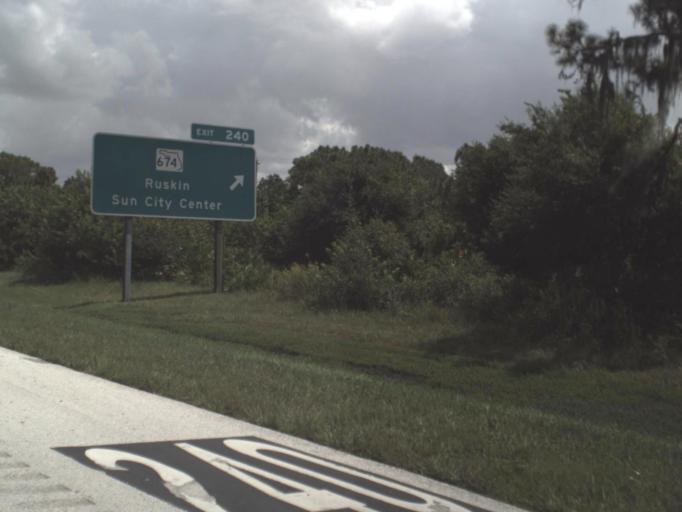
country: US
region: Florida
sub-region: Hillsborough County
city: Sun City Center
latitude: 27.7053
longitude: -82.3899
